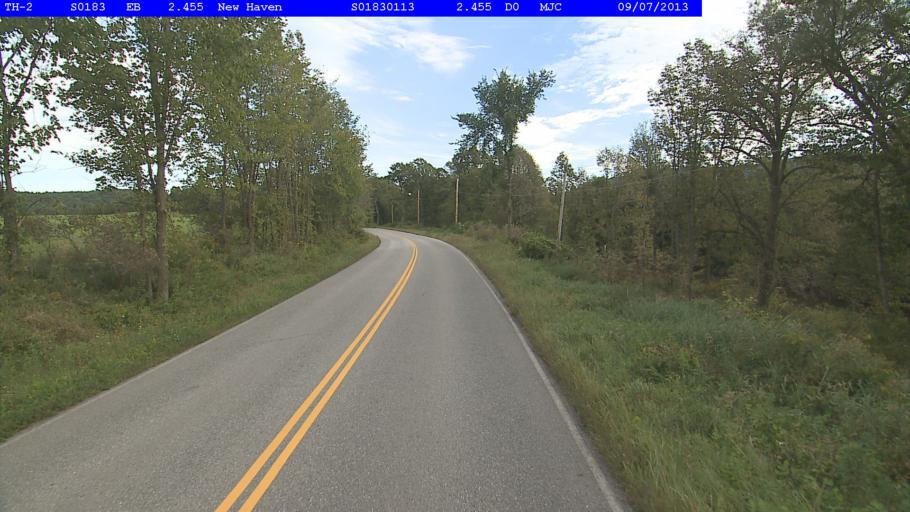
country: US
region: Vermont
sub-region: Addison County
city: Middlebury (village)
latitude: 44.0750
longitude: -73.1301
